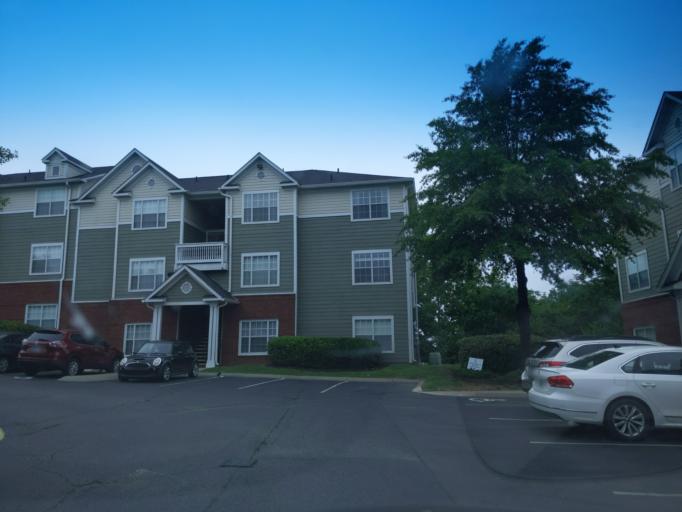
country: US
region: Tennessee
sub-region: Williamson County
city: Brentwood
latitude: 36.0346
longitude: -86.7740
